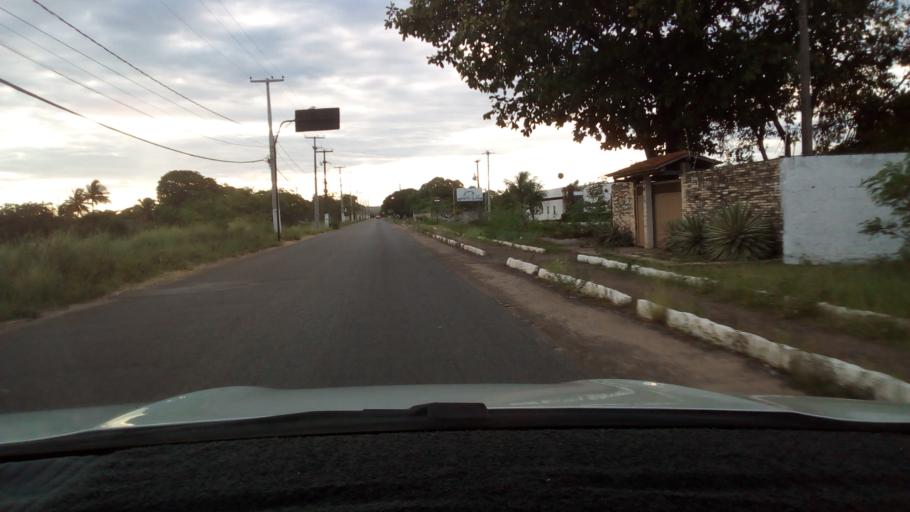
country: BR
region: Paraiba
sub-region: Cabedelo
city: Cabedelo
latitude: -7.0413
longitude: -34.8471
